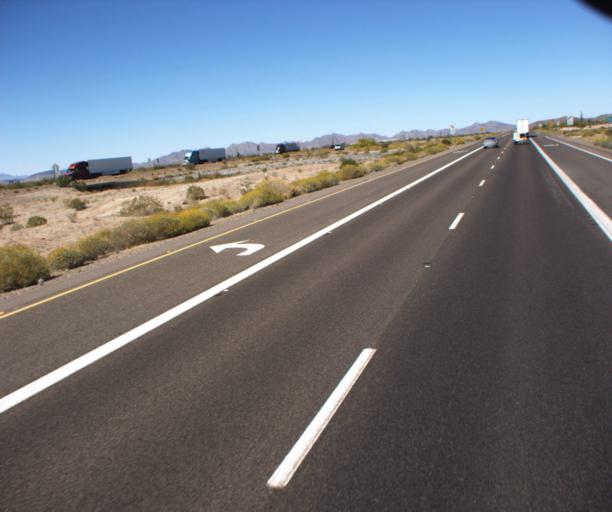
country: US
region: Arizona
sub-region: Maricopa County
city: Gila Bend
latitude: 33.1295
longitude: -112.6501
